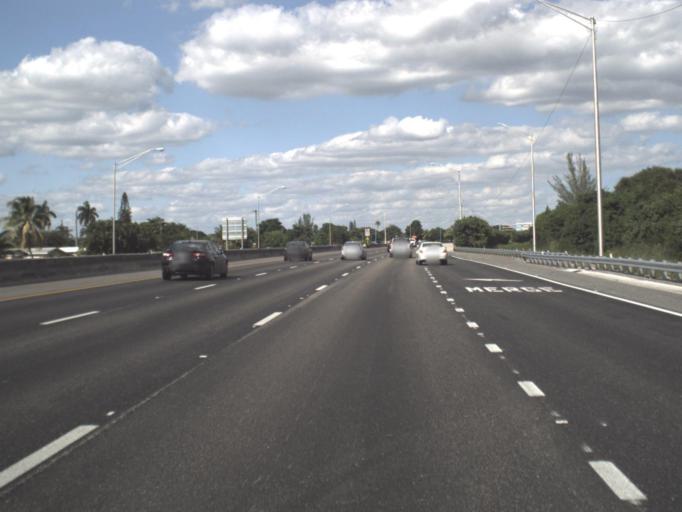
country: US
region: Florida
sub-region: Broward County
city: Miramar
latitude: 25.9847
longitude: -80.2296
